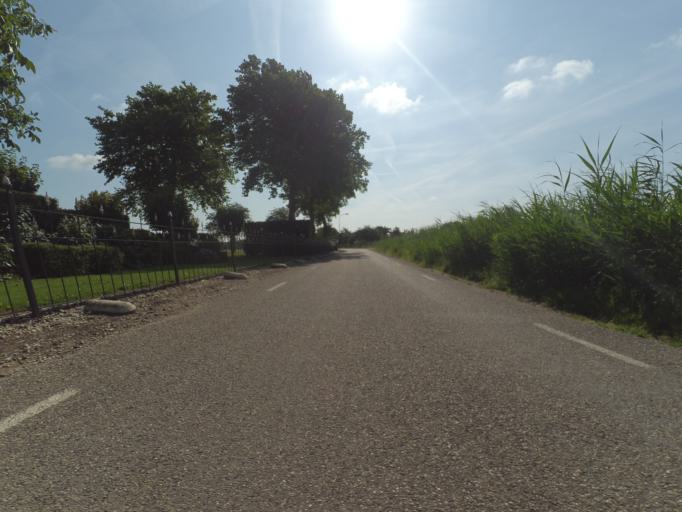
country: NL
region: Utrecht
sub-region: Gemeente Wijk bij Duurstede
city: Wijk bij Duurstede
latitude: 51.9974
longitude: 5.2944
